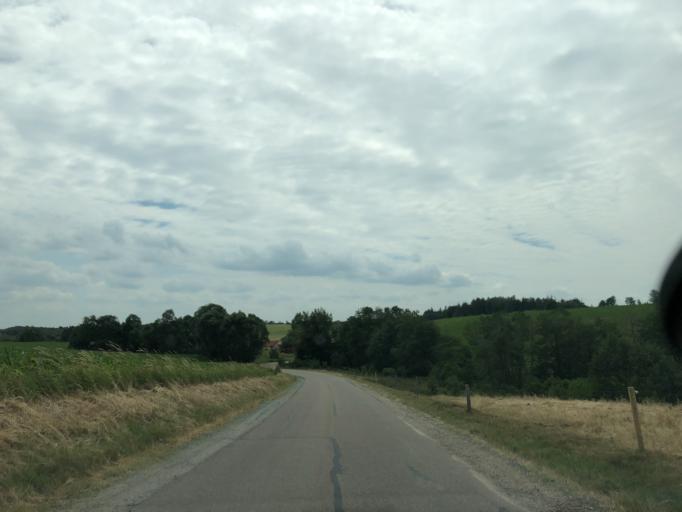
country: DK
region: Central Jutland
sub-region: Silkeborg Kommune
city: Svejbaek
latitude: 56.2018
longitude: 9.6900
